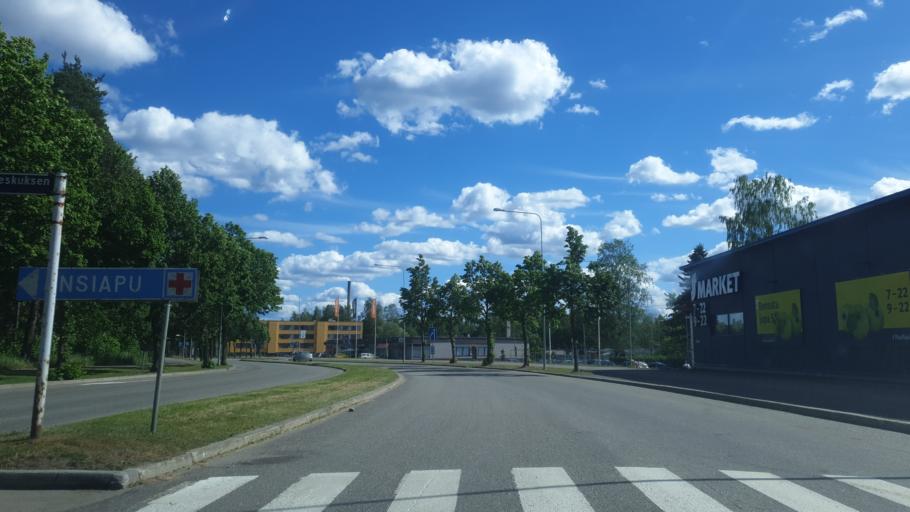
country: FI
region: Northern Savo
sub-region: Varkaus
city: Varkaus
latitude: 62.3286
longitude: 27.8892
